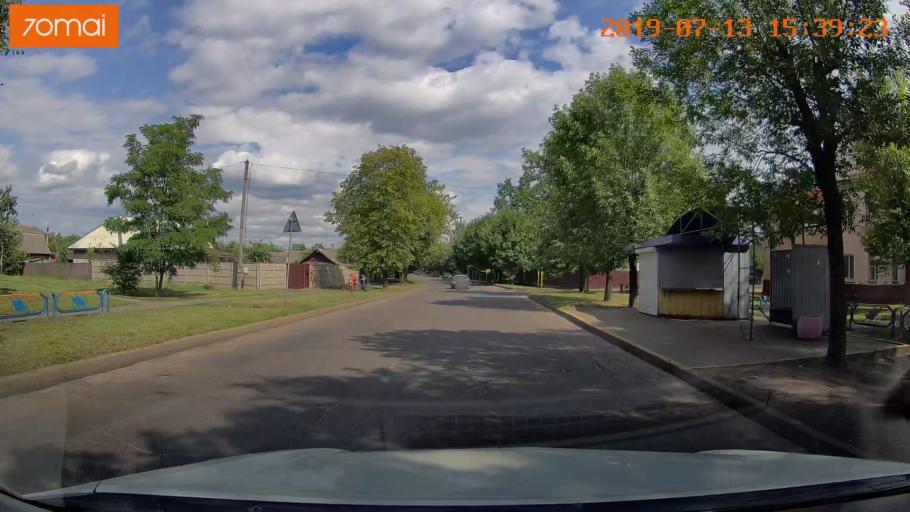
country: BY
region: Mogilev
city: Babruysk
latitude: 53.1354
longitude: 29.1803
